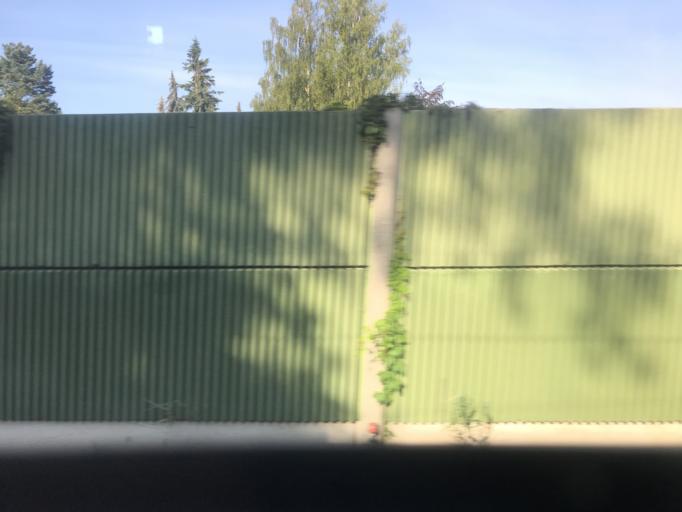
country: CZ
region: Jihocesky
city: Plana nad Luznici
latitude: 49.3441
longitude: 14.7104
